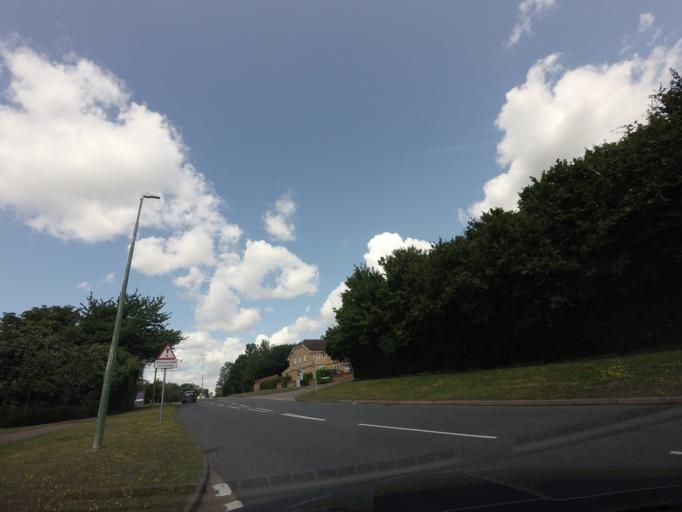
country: GB
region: England
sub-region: Kent
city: Boxley
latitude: 51.2763
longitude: 0.5588
